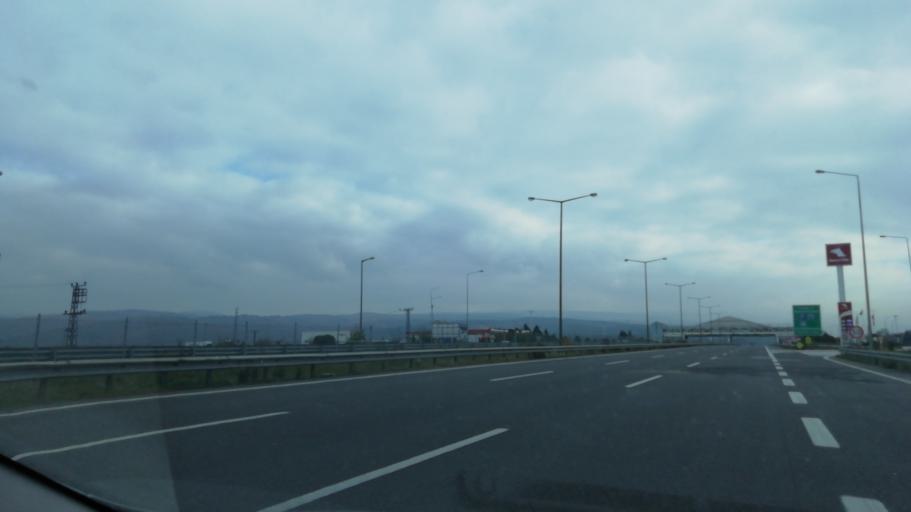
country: TR
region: Duzce
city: Duzce
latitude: 40.7905
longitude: 31.2359
